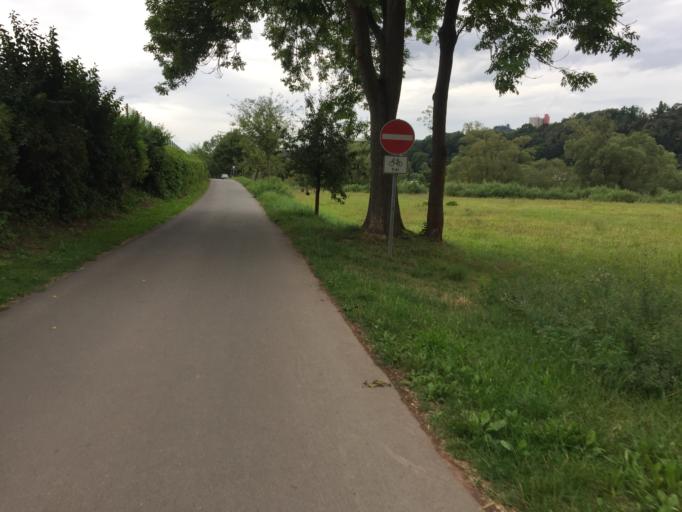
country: DE
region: Hesse
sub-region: Regierungsbezirk Kassel
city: Rotenburg an der Fulda
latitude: 50.9911
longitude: 9.7467
